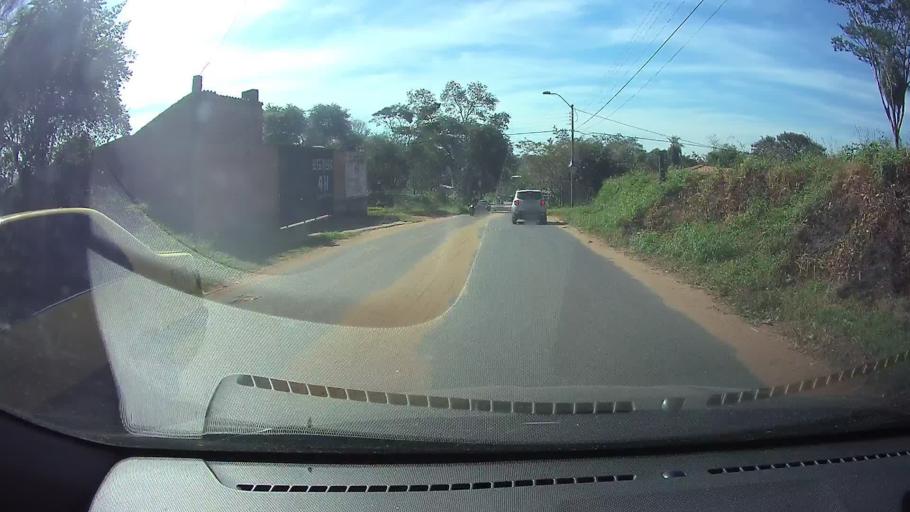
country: PY
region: Central
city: Villa Elisa
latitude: -25.3721
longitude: -57.5720
